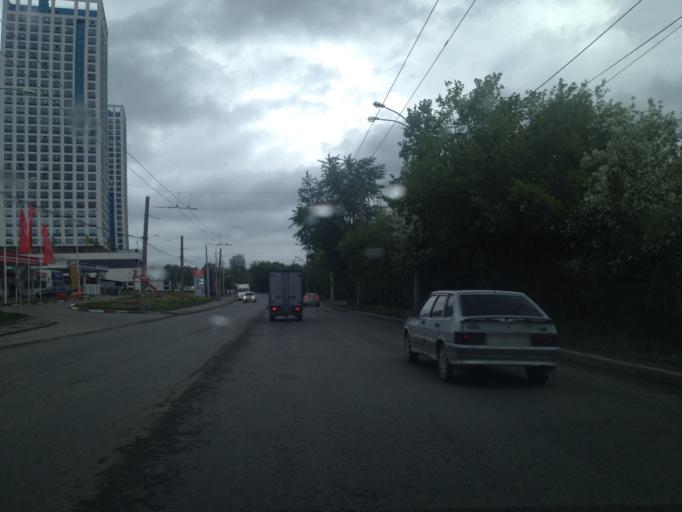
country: RU
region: Sverdlovsk
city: Yekaterinburg
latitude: 56.7755
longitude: 60.6653
